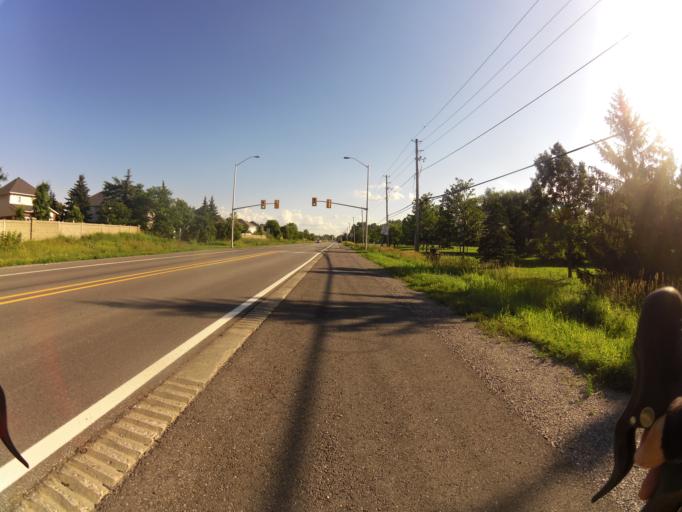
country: CA
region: Ontario
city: Ottawa
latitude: 45.2756
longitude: -75.6963
